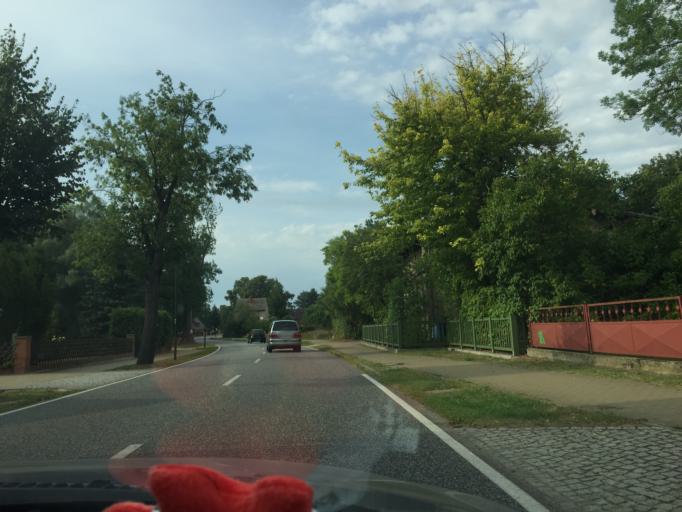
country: DE
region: Brandenburg
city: Liebenwalde
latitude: 52.8629
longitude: 13.3975
